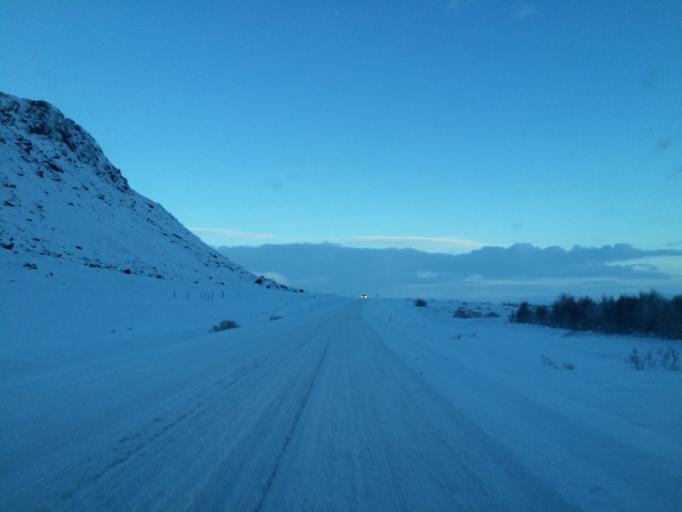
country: IS
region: South
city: Selfoss
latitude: 63.9589
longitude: -21.0094
